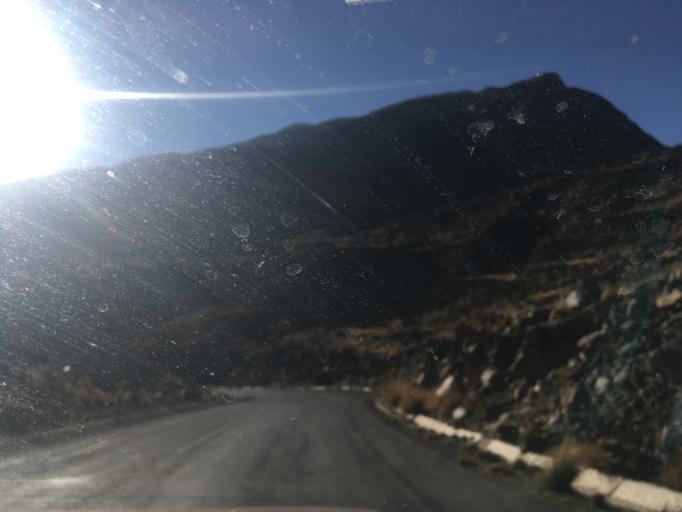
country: BO
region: La Paz
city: Quime
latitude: -17.0277
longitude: -67.2854
